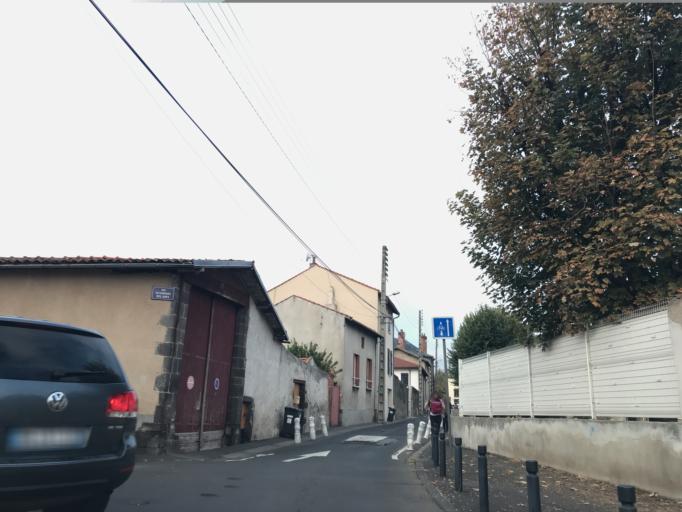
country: FR
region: Auvergne
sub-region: Departement du Puy-de-Dome
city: Clermont-Ferrand
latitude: 45.7957
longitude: 3.1146
